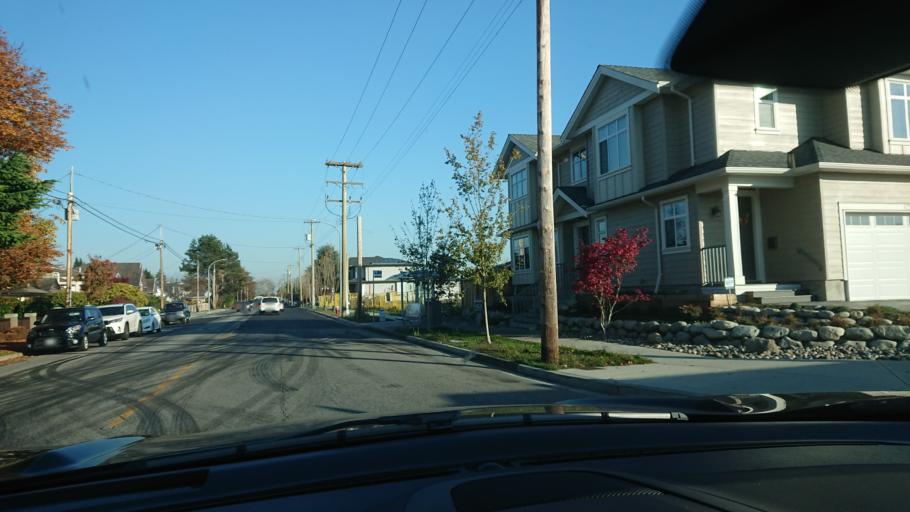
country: CA
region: British Columbia
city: Richmond
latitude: 49.1251
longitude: -123.1645
